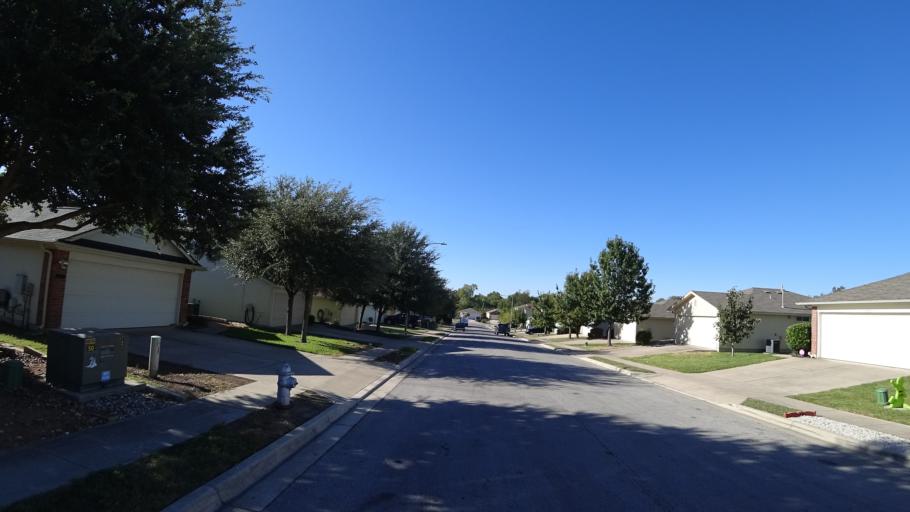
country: US
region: Texas
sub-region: Travis County
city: Austin
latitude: 30.2907
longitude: -97.6687
